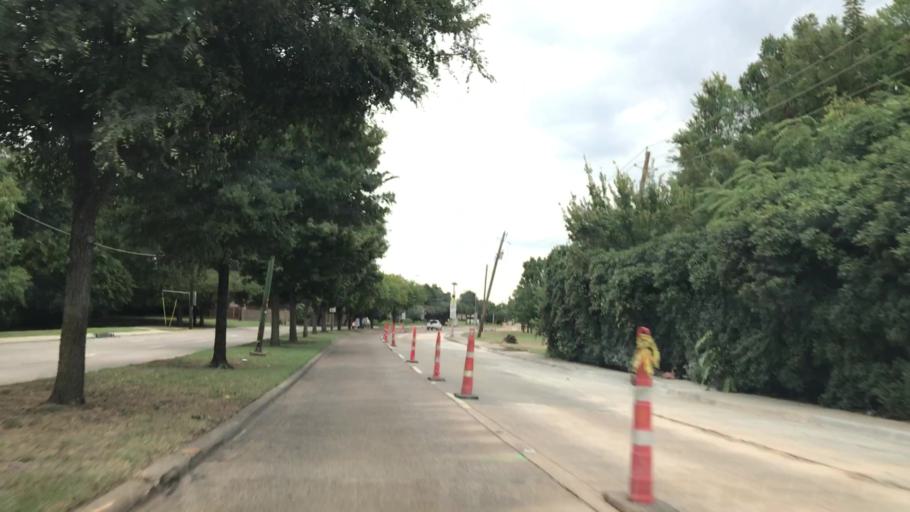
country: US
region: Texas
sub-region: Dallas County
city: Addison
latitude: 32.9625
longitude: -96.7961
